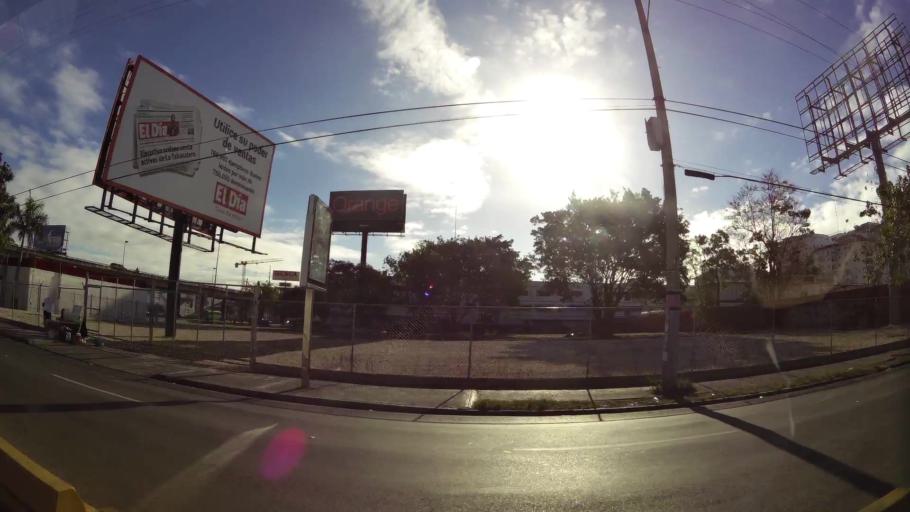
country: DO
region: Nacional
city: La Julia
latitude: 18.4822
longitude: -69.9311
